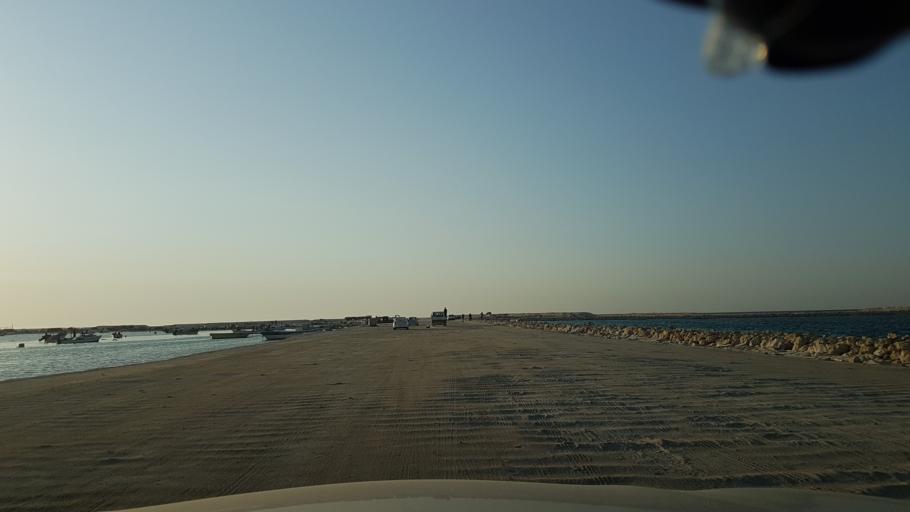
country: BH
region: Manama
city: Jidd Hafs
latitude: 26.2530
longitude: 50.5012
